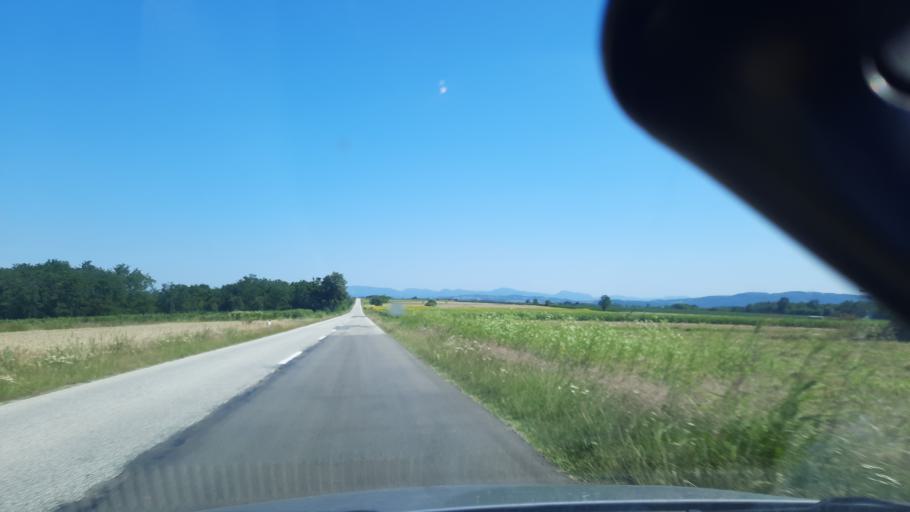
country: RS
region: Central Serbia
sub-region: Branicevski Okrug
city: Malo Crnice
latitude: 44.5736
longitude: 21.4242
